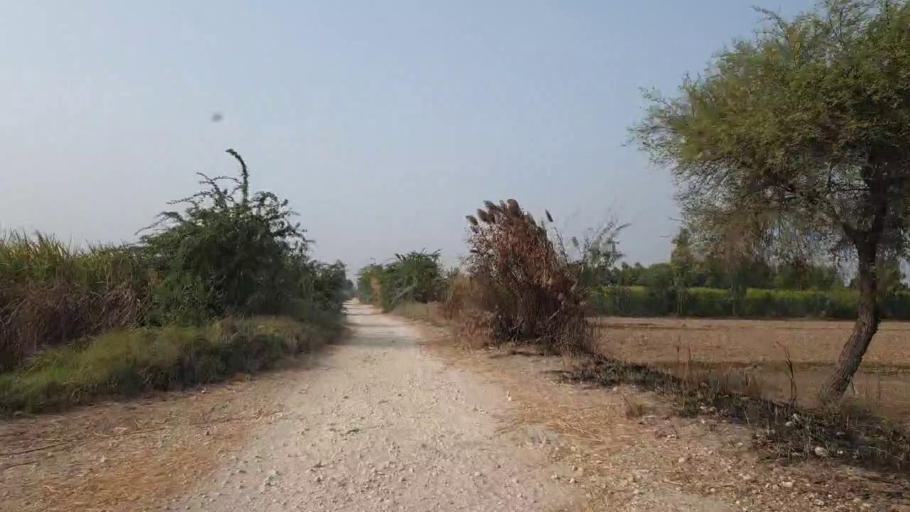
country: PK
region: Sindh
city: Tando Muhammad Khan
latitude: 25.0794
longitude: 68.5891
